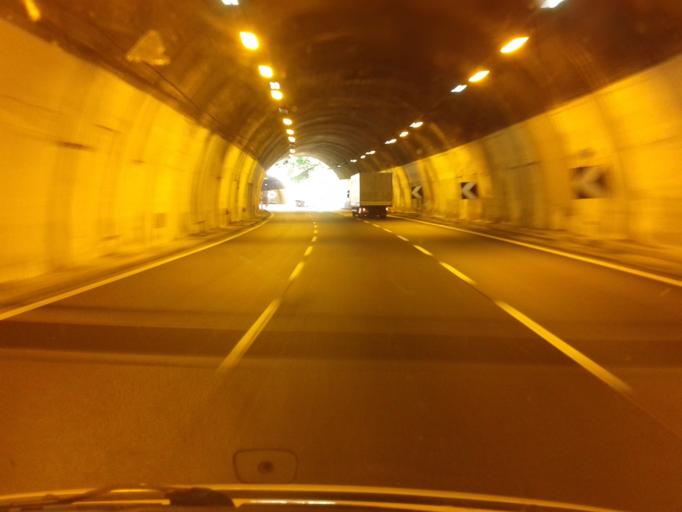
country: IT
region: Liguria
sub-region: Provincia di Genova
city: Rossiglione
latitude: 44.5612
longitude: 8.6668
